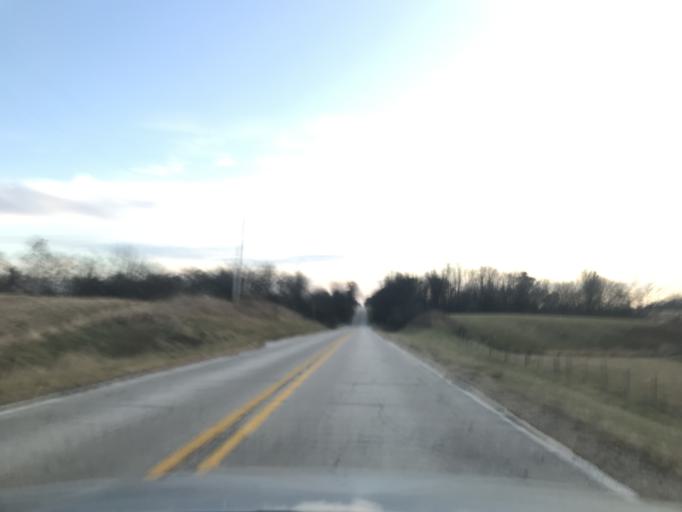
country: US
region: Illinois
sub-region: Henderson County
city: Oquawka
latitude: 40.9624
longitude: -90.8640
